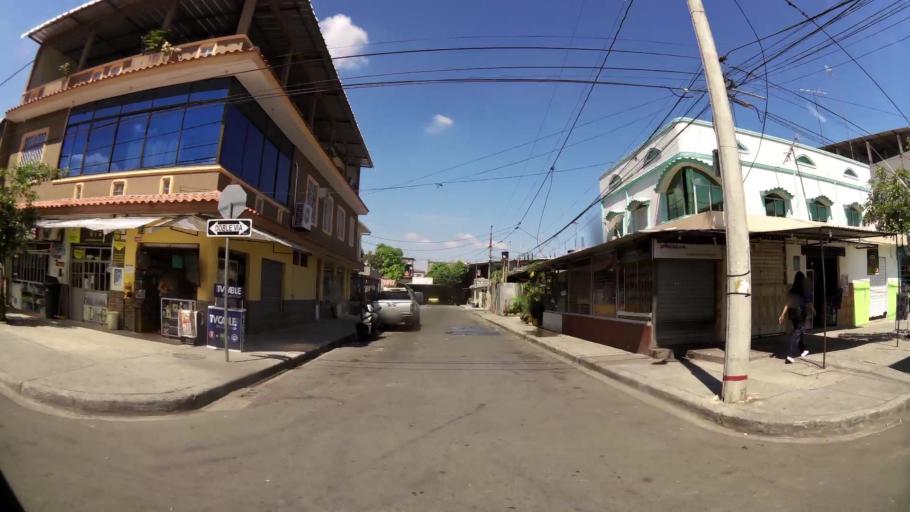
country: EC
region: Guayas
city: Guayaquil
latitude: -2.1901
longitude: -79.9441
